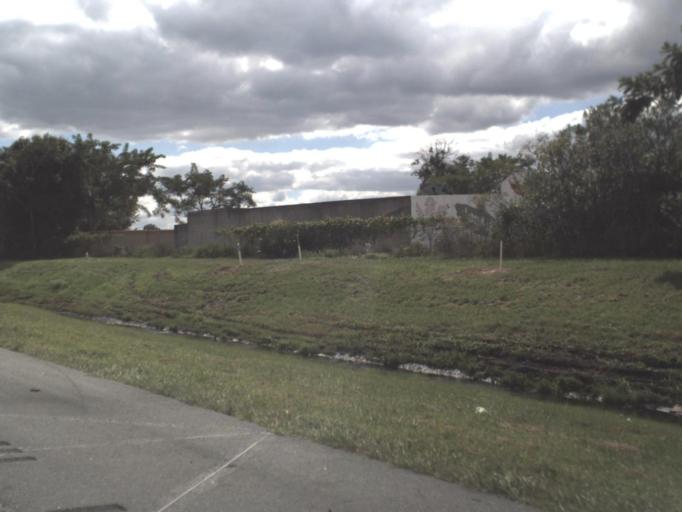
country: US
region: Florida
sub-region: Orange County
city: Gotha
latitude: 28.5173
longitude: -81.5040
